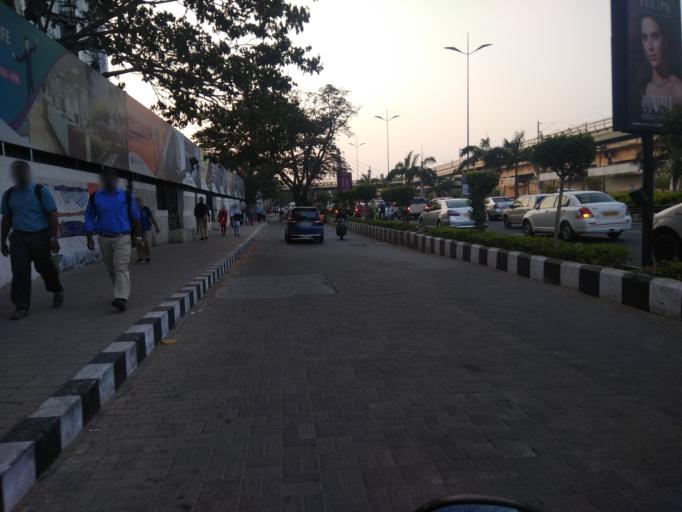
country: IN
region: Tamil Nadu
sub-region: Chennai
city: Gandhi Nagar
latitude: 12.9907
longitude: 80.2505
